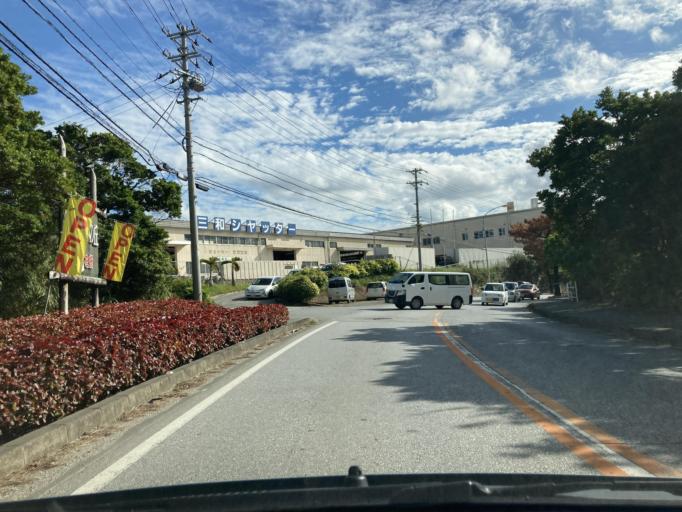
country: JP
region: Okinawa
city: Ishikawa
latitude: 26.4296
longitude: 127.8078
